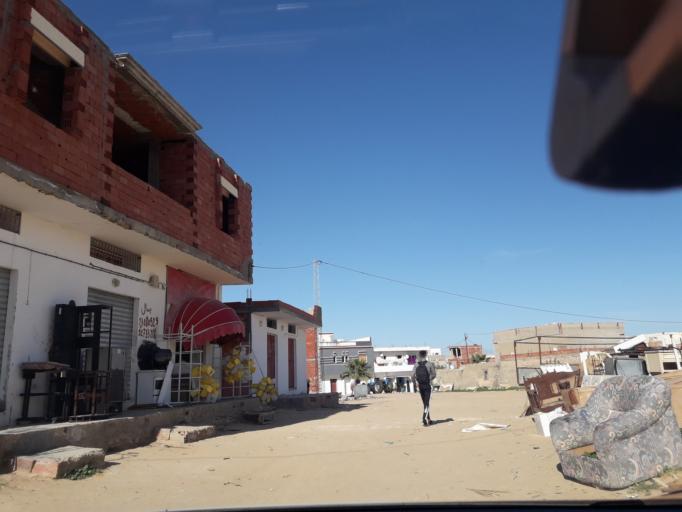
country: TN
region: Safaqis
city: Sfax
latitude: 34.7403
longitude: 10.5255
